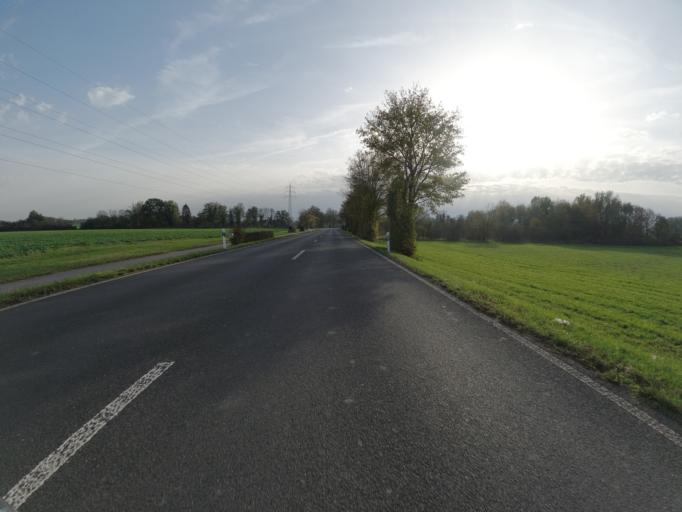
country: DE
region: North Rhine-Westphalia
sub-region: Regierungsbezirk Dusseldorf
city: Moers
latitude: 51.4325
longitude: 6.6196
